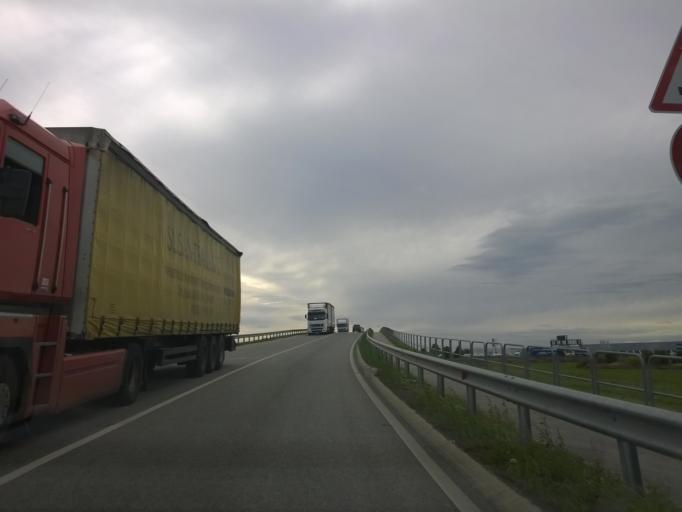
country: HU
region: Pest
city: Szigetszentmiklos
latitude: 47.3815
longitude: 19.0332
